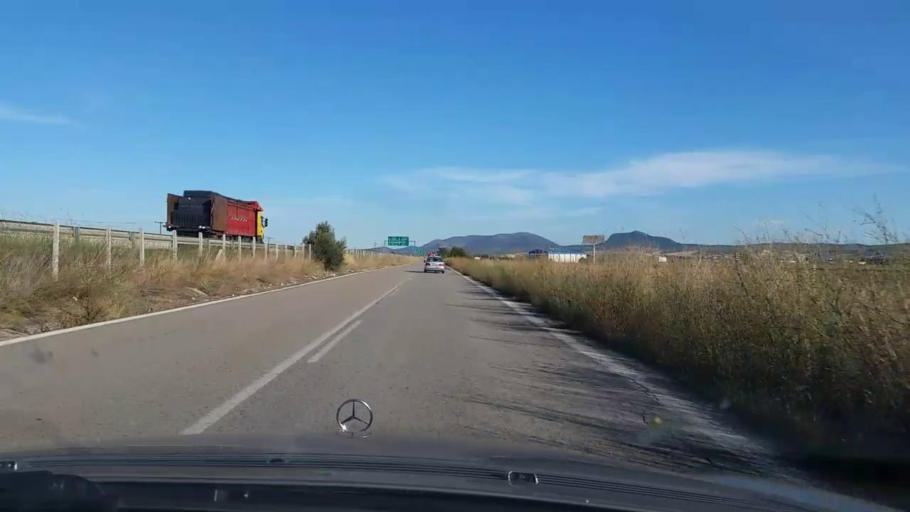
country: GR
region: Central Greece
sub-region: Nomos Voiotias
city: Thivai
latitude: 38.3667
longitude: 23.3037
